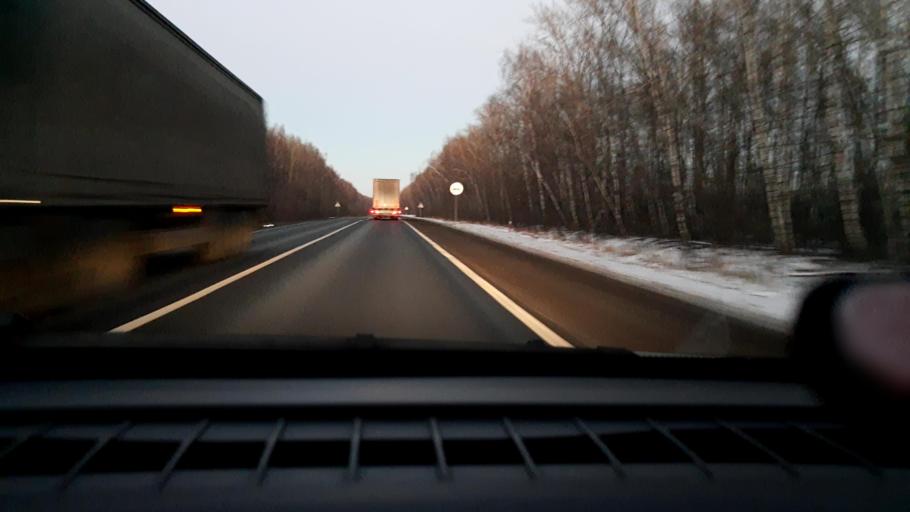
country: RU
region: Nizjnij Novgorod
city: Pervoye Maya
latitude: 55.9989
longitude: 44.8231
